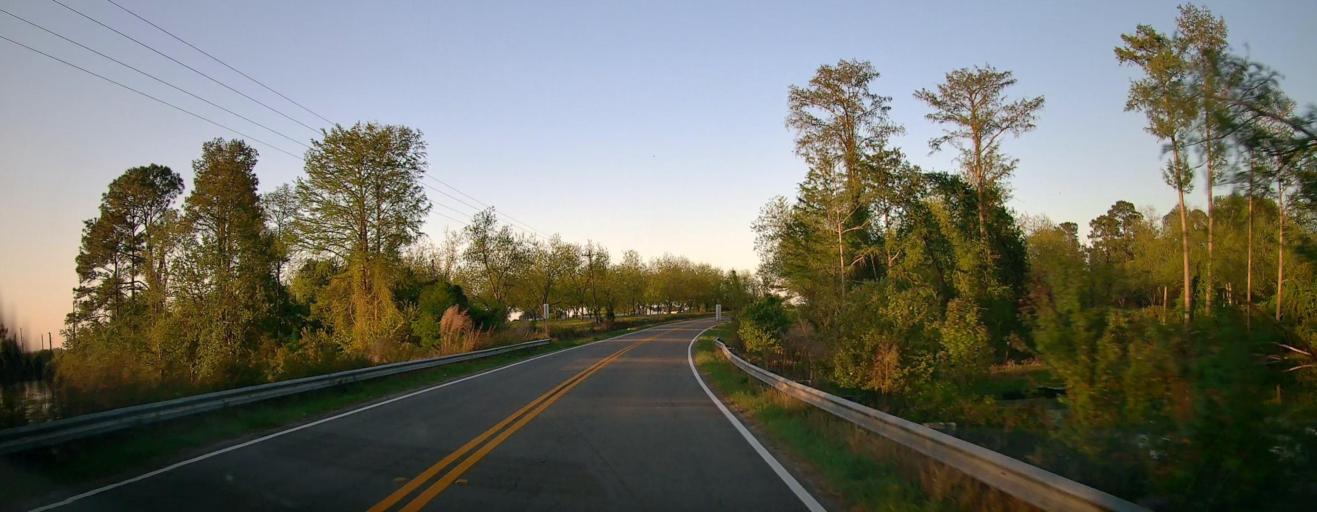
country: US
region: Georgia
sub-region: Irwin County
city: Ocilla
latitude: 31.6391
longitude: -83.2745
